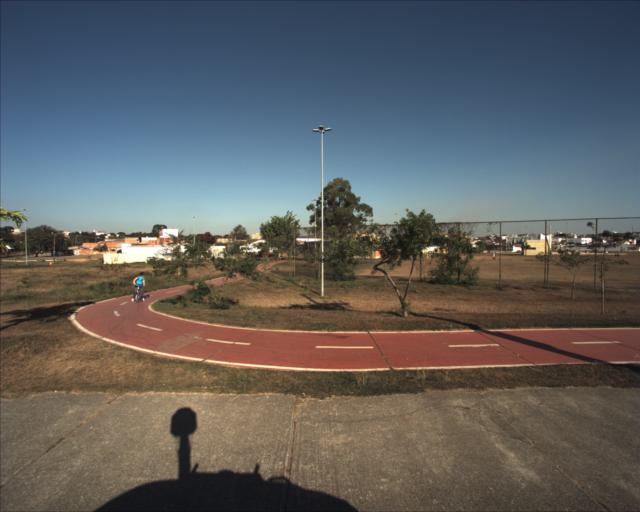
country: BR
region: Sao Paulo
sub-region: Sorocaba
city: Sorocaba
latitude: -23.4678
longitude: -47.4437
